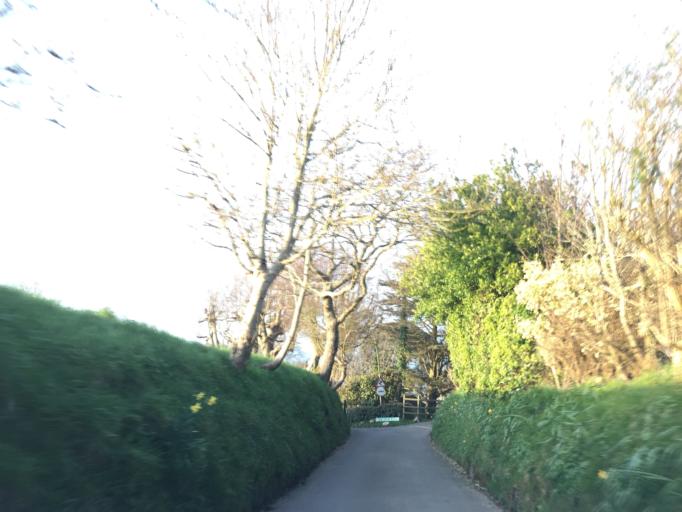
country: JE
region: St Helier
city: Saint Helier
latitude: 49.2296
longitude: -2.0495
